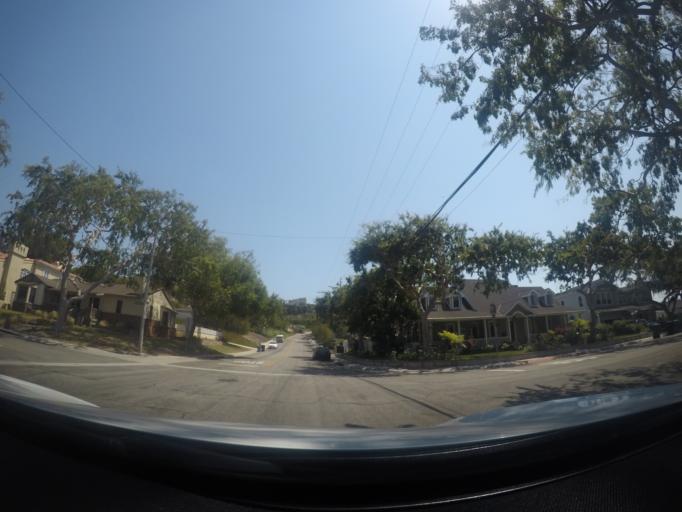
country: US
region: California
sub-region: Los Angeles County
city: Palos Verdes Estates
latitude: 33.8192
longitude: -118.3698
